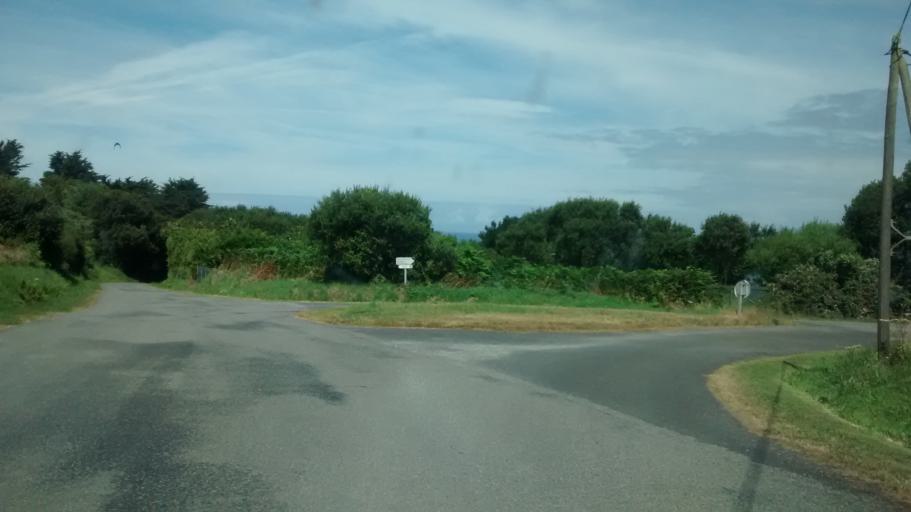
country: FR
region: Brittany
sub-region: Departement du Finistere
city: Plouguerneau
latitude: 48.6210
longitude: -4.4799
